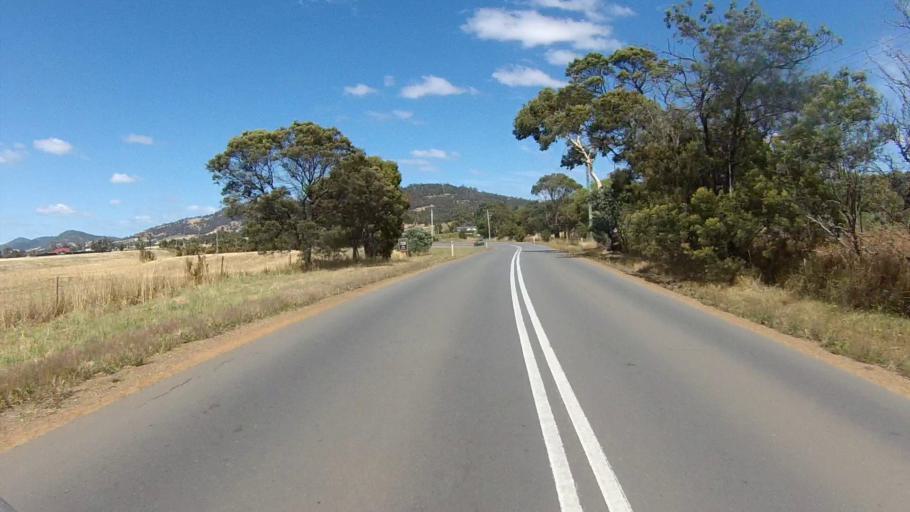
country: AU
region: Tasmania
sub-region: Clarence
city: Cambridge
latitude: -42.7709
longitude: 147.4158
